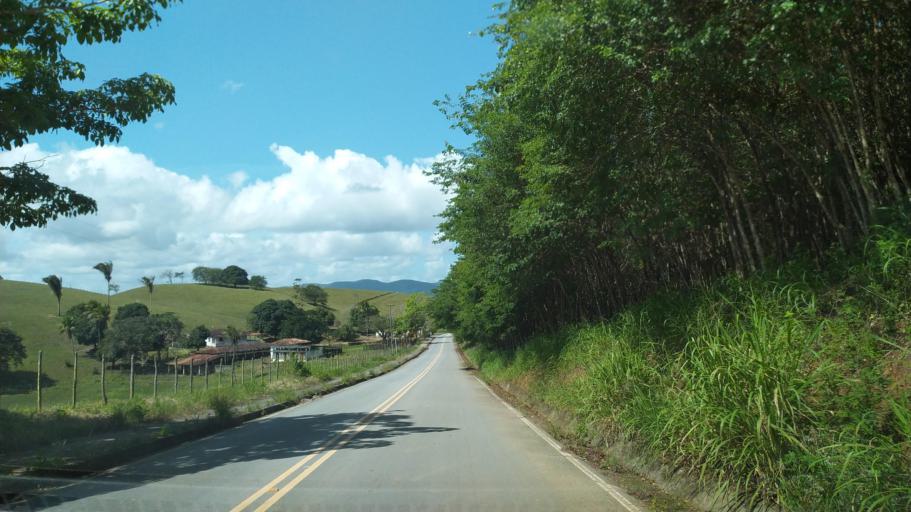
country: BR
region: Alagoas
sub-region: Uniao Dos Palmares
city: Uniao dos Palmares
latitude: -9.1623
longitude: -36.0707
